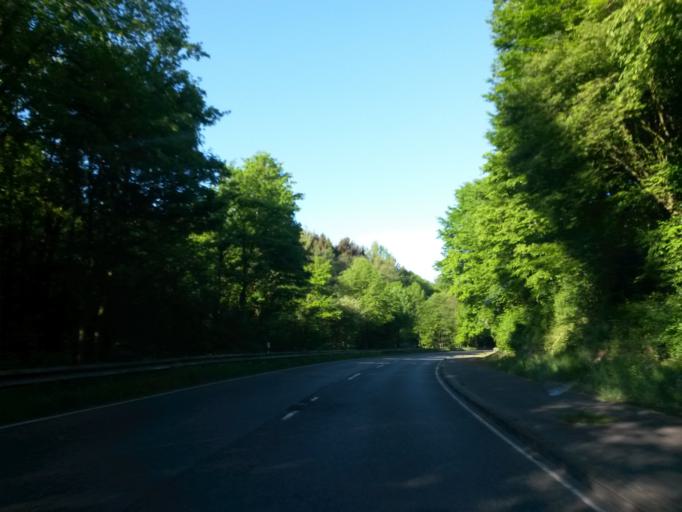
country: DE
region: North Rhine-Westphalia
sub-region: Regierungsbezirk Koln
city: Much
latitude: 50.8960
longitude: 7.3900
